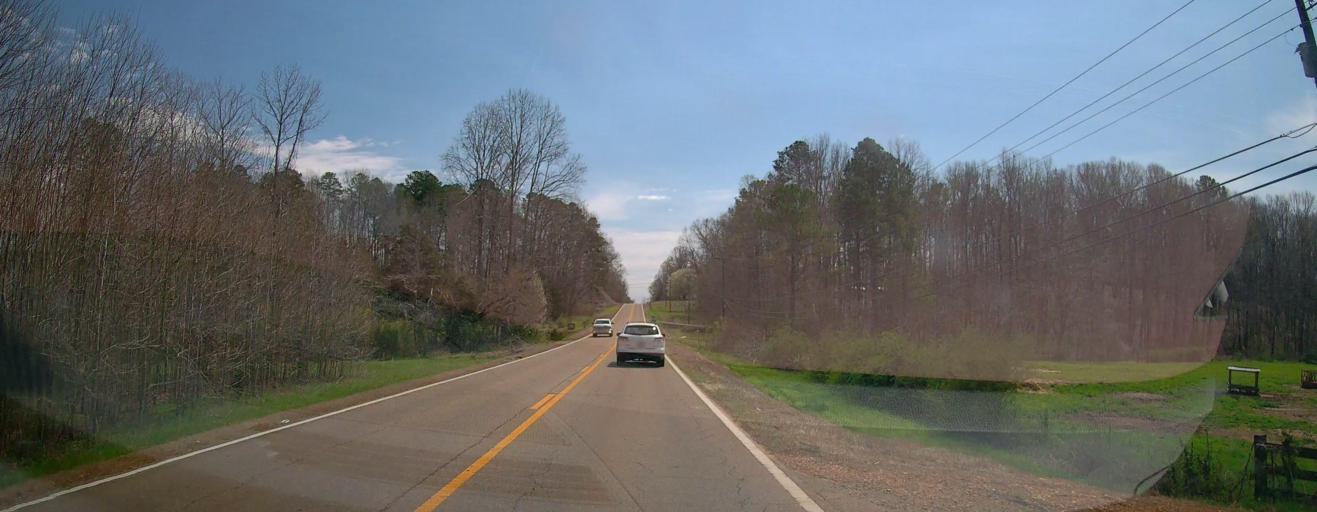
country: US
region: Mississippi
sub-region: Union County
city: New Albany
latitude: 34.4435
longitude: -88.9640
